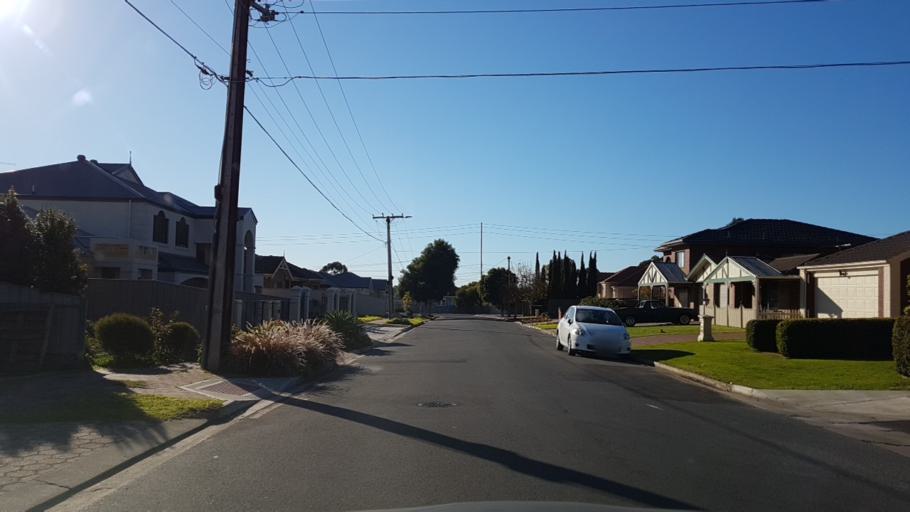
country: AU
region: South Australia
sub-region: Campbelltown
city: Paradise
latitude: -34.8776
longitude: 138.6790
